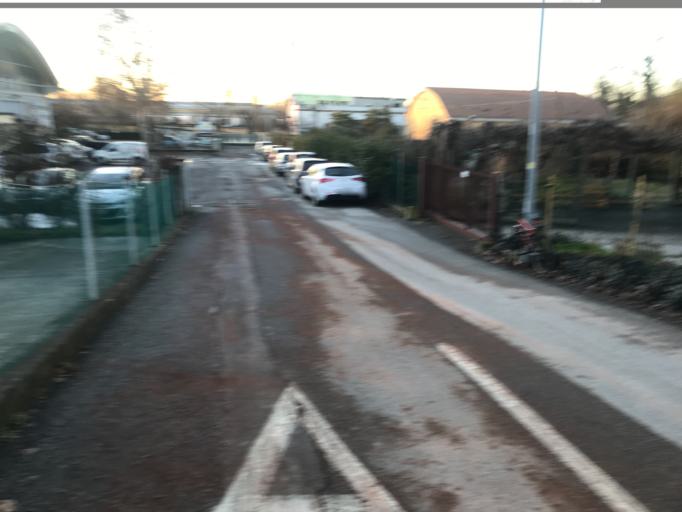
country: IT
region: Emilia-Romagna
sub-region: Provincia di Bologna
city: Progresso
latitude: 44.5418
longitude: 11.3516
